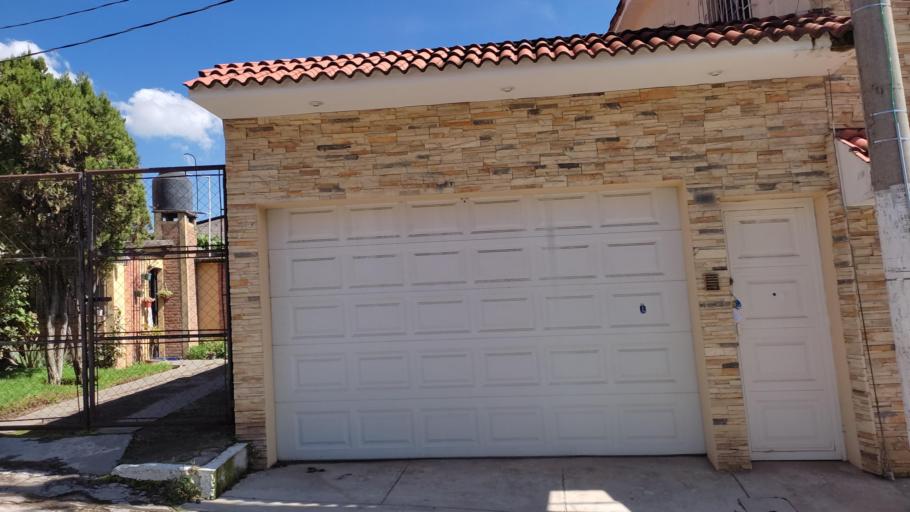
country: GT
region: Quetzaltenango
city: Quetzaltenango
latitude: 14.8561
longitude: -91.5225
